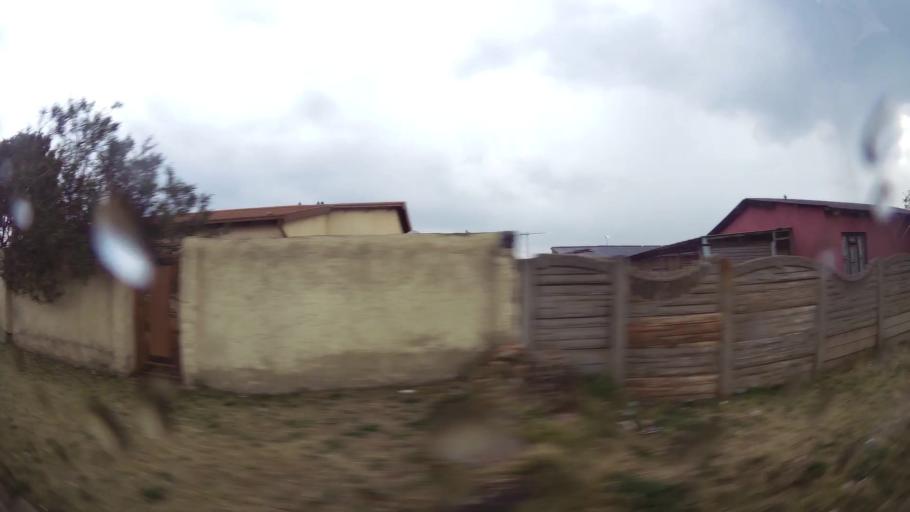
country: ZA
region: Gauteng
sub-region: Ekurhuleni Metropolitan Municipality
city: Germiston
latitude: -26.3642
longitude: 28.1648
